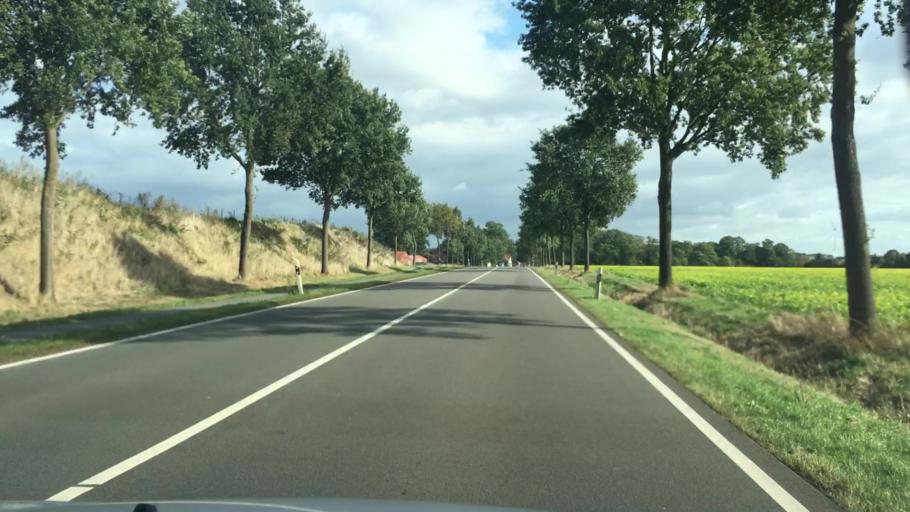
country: DE
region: Lower Saxony
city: Rehden
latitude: 52.6120
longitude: 8.4697
